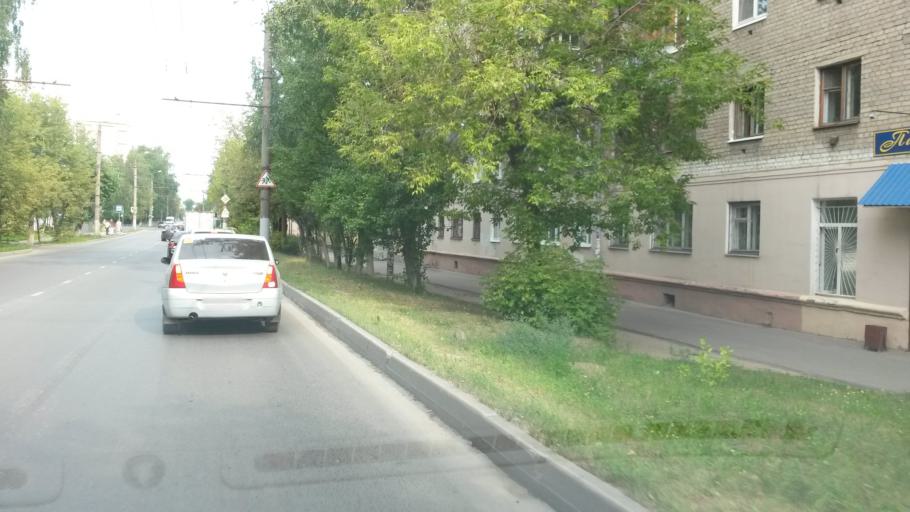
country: RU
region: Ivanovo
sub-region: Gorod Ivanovo
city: Ivanovo
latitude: 57.0031
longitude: 40.9585
